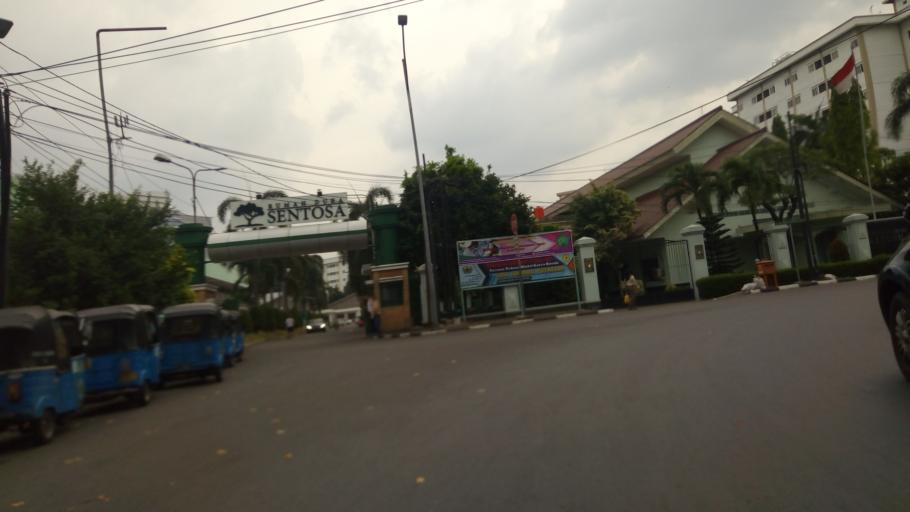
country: ID
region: Jakarta Raya
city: Jakarta
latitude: -6.1756
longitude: 106.8366
